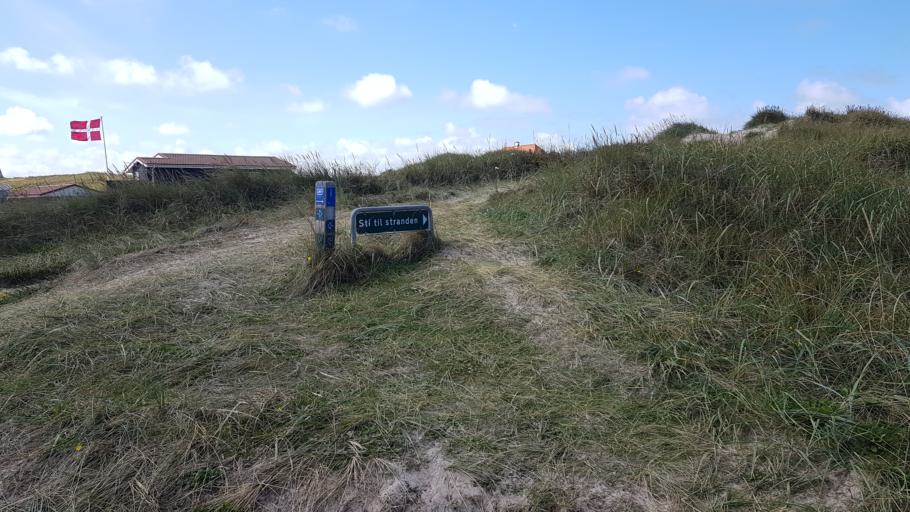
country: DK
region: North Denmark
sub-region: Jammerbugt Kommune
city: Pandrup
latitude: 57.3779
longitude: 9.7167
